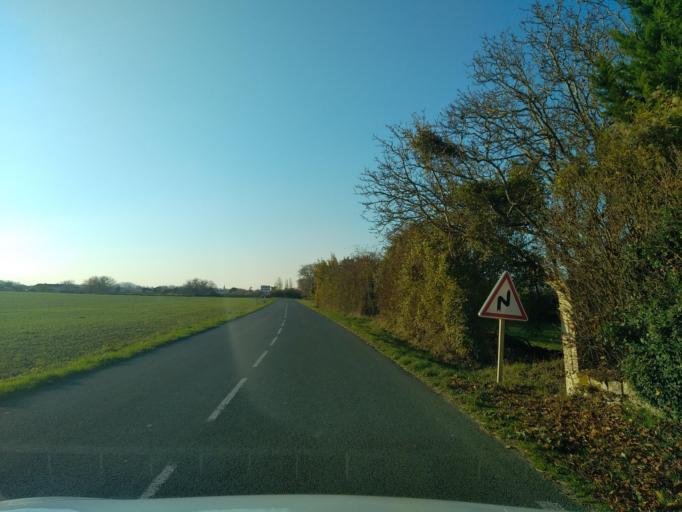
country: FR
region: Pays de la Loire
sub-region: Departement de la Vendee
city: Maillezais
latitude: 46.3402
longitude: -0.7723
